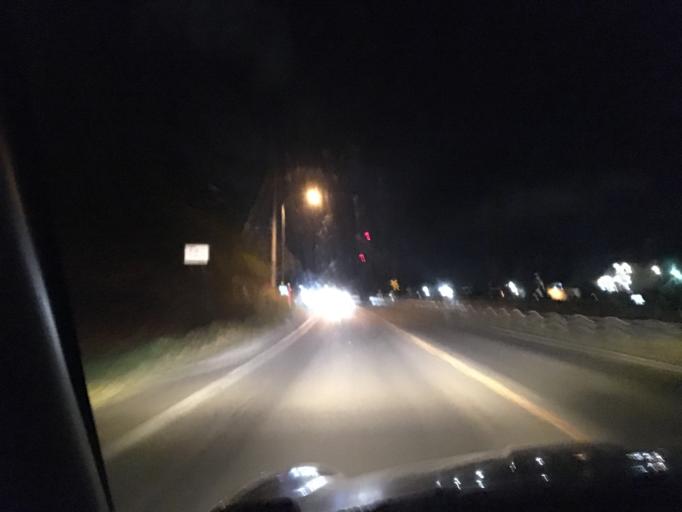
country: JP
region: Hokkaido
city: Muroran
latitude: 42.3591
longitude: 140.9725
